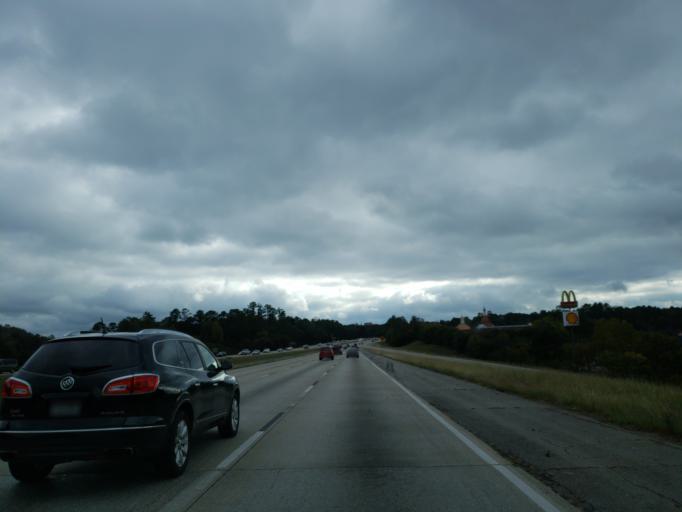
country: US
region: Alabama
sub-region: Jefferson County
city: Vestavia Hills
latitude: 33.4119
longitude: -86.7595
